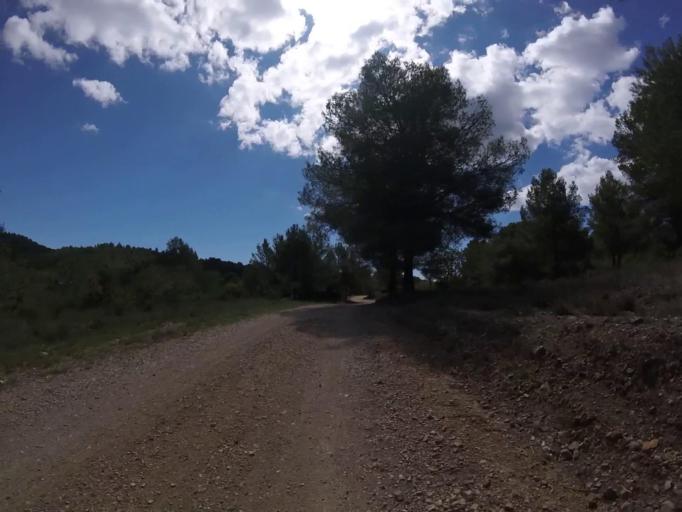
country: ES
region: Valencia
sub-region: Provincia de Castello
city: Santa Magdalena de Pulpis
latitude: 40.3181
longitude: 0.3319
